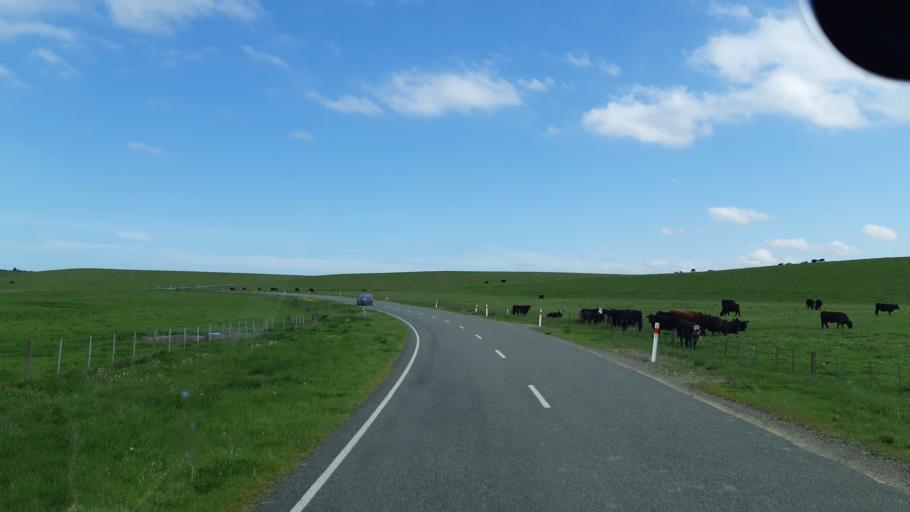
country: NZ
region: Canterbury
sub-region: Timaru District
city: Pleasant Point
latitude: -44.1795
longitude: 171.2074
